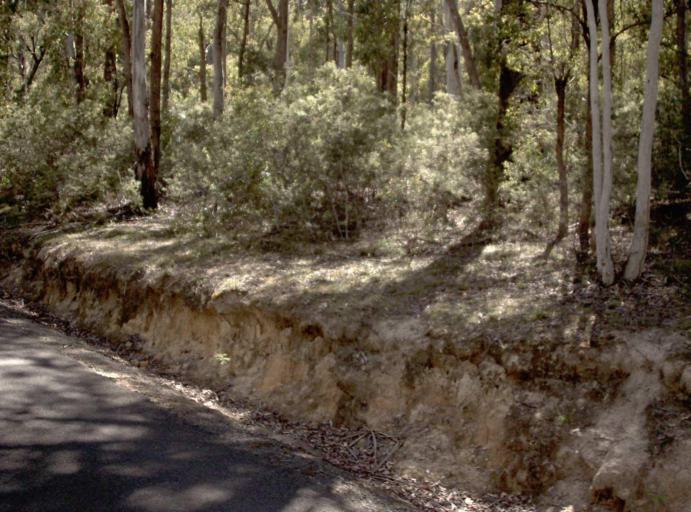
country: AU
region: New South Wales
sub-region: Bombala
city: Bombala
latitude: -37.1209
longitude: 148.7515
